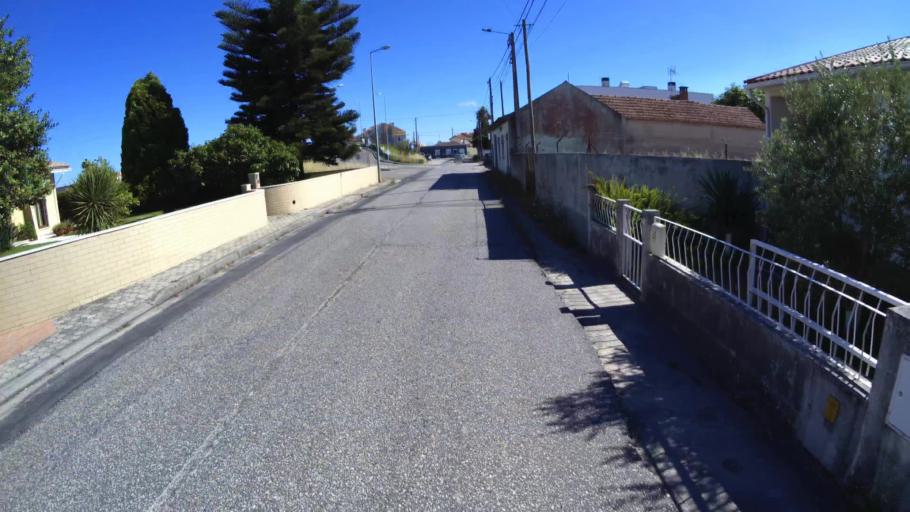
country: PT
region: Aveiro
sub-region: Aveiro
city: Aveiro
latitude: 40.6569
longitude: -8.6236
